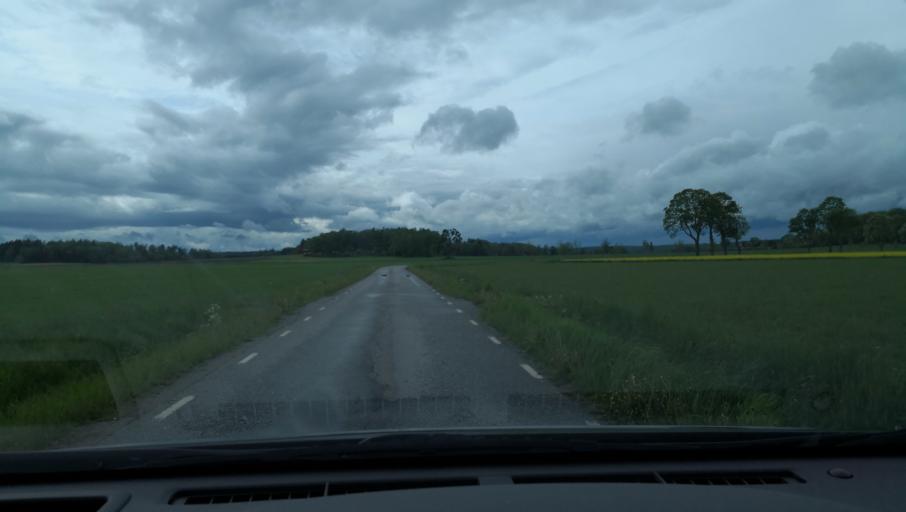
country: SE
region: Uppsala
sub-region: Enkopings Kommun
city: Orsundsbro
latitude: 59.7206
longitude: 17.4229
